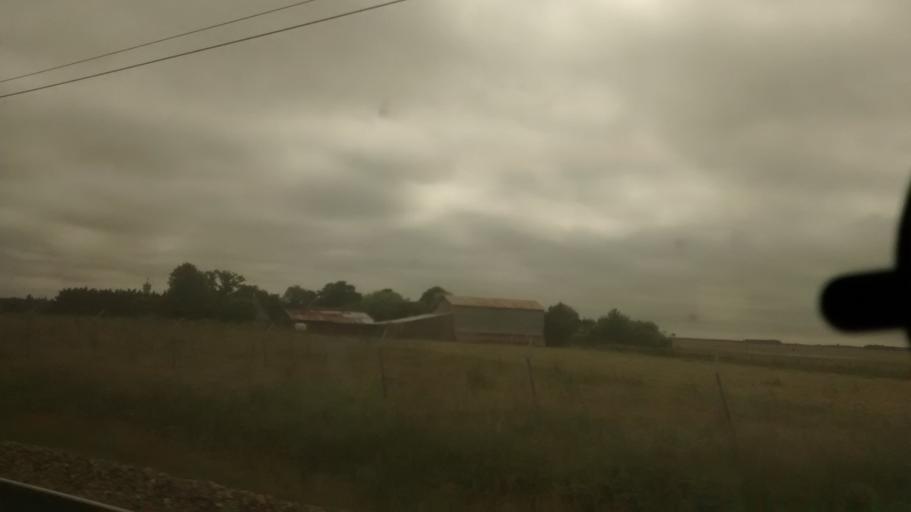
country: FR
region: Centre
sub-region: Departement d'Eure-et-Loir
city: Arrou
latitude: 48.1115
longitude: 1.1711
